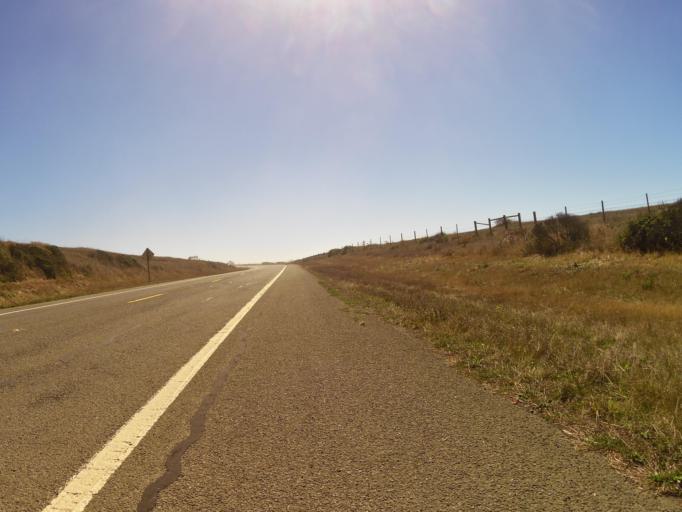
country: US
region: California
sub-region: Mendocino County
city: Fort Bragg
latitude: 39.6742
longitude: -123.7904
